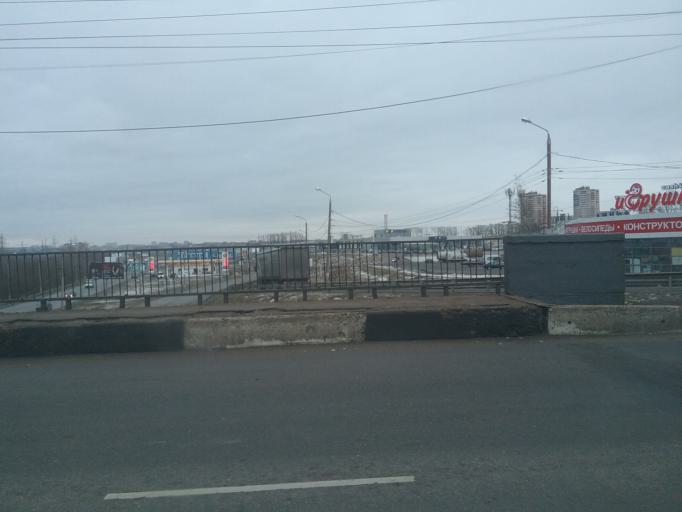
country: RU
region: Tula
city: Tula
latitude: 54.1716
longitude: 37.6372
